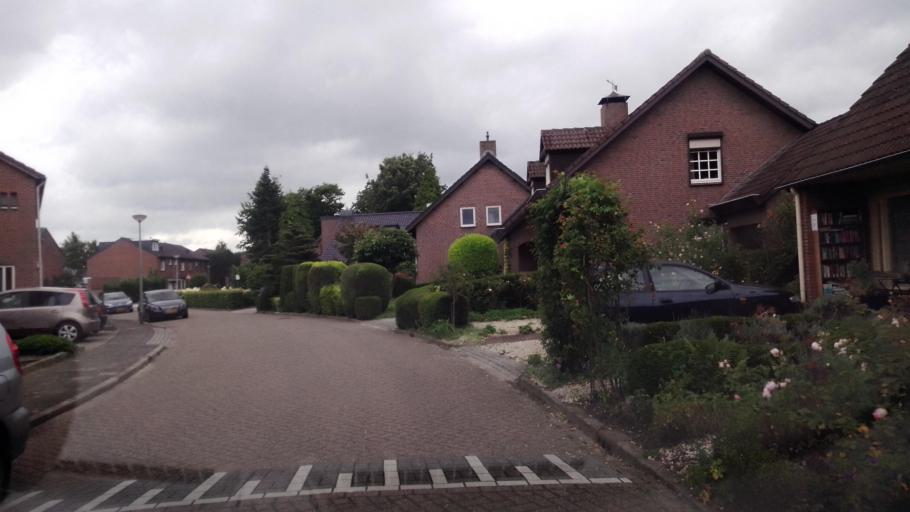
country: NL
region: Limburg
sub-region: Gemeente Peel en Maas
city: Maasbree
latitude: 51.3613
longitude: 6.0492
